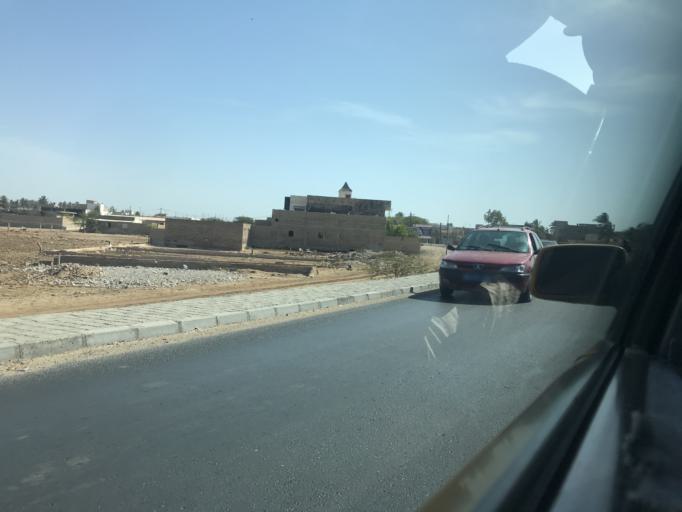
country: SN
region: Saint-Louis
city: Saint-Louis
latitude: 16.0371
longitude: -16.4670
